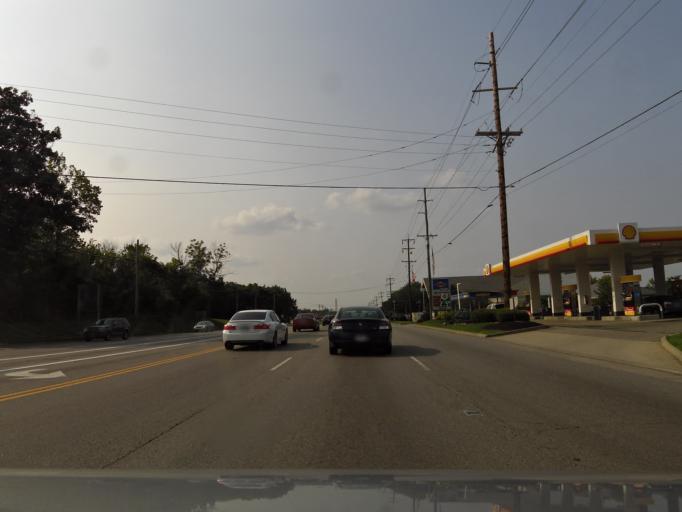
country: US
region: Ohio
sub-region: Hamilton County
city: Springdale
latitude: 39.3016
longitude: -84.4852
